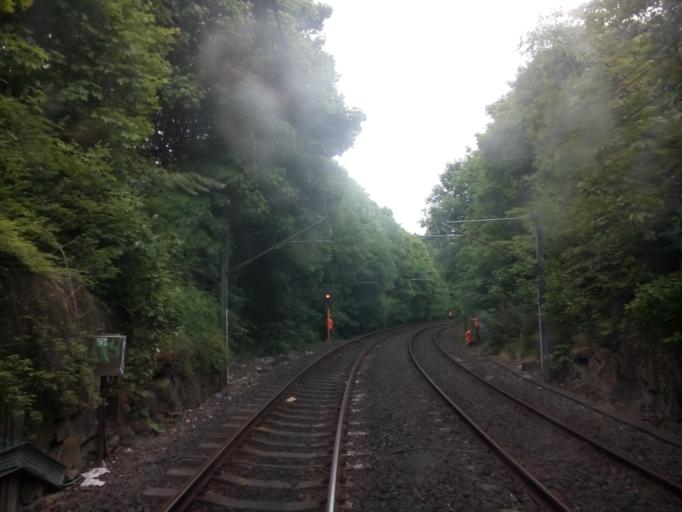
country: GB
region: England
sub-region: Gateshead
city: Felling
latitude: 54.9760
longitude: -1.5788
